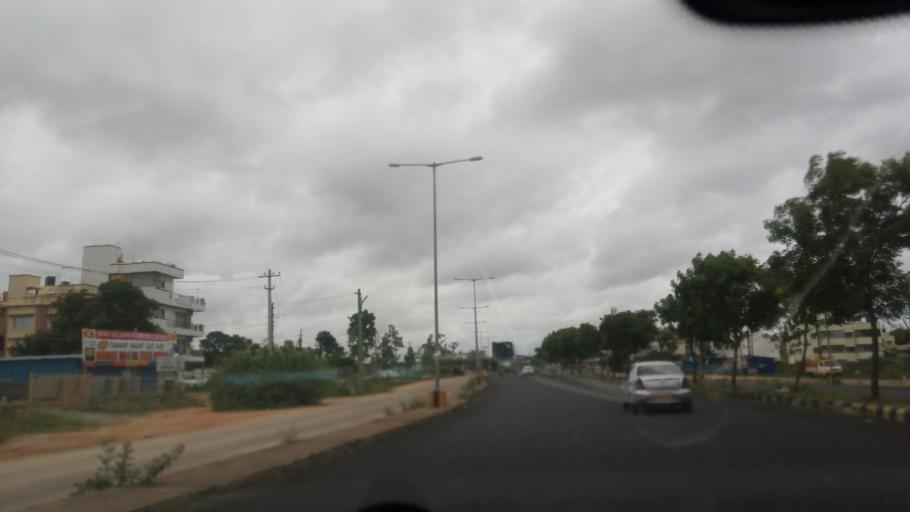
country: IN
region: Karnataka
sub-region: Mysore
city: Mysore
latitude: 12.3286
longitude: 76.5975
